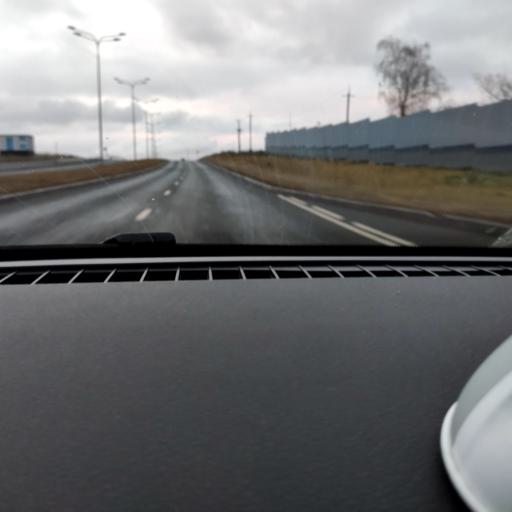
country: RU
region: Samara
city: Samara
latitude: 53.2849
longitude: 50.2361
